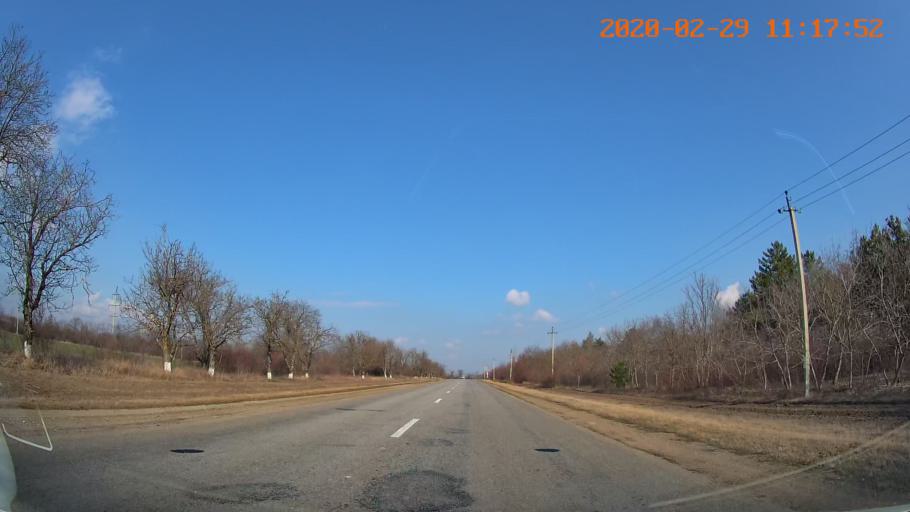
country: MD
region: Telenesti
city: Dubasari
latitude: 47.3274
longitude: 29.1716
